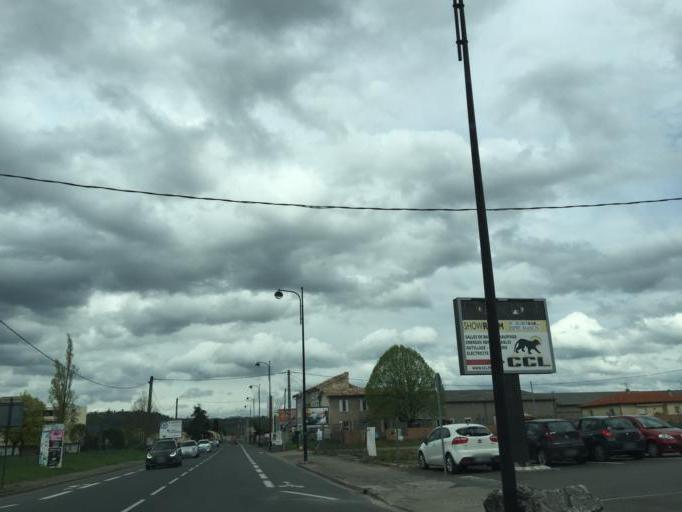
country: FR
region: Midi-Pyrenees
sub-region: Departement du Tarn
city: Albi
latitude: 43.9462
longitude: 2.1516
